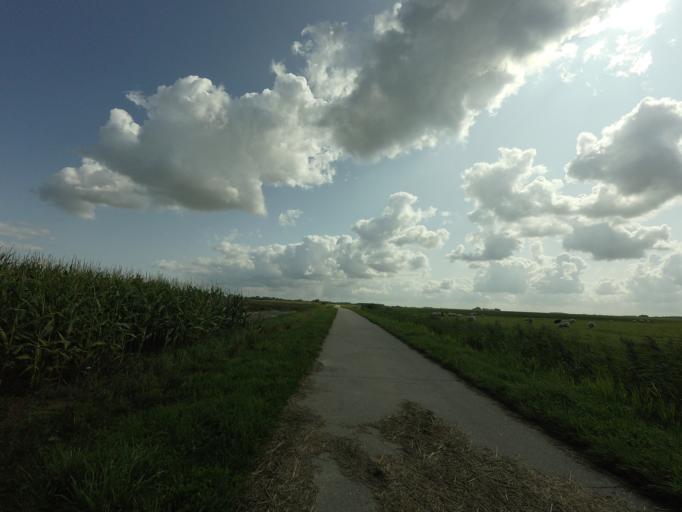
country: NL
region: Friesland
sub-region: Gemeente Het Bildt
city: Sint Jacobiparochie
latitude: 53.2676
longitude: 5.6124
